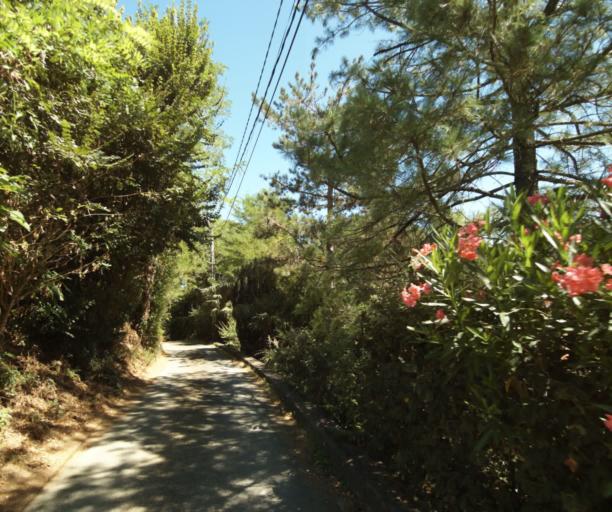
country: FR
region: Midi-Pyrenees
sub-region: Departement de la Haute-Garonne
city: Castanet-Tolosan
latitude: 43.5103
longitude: 1.4927
